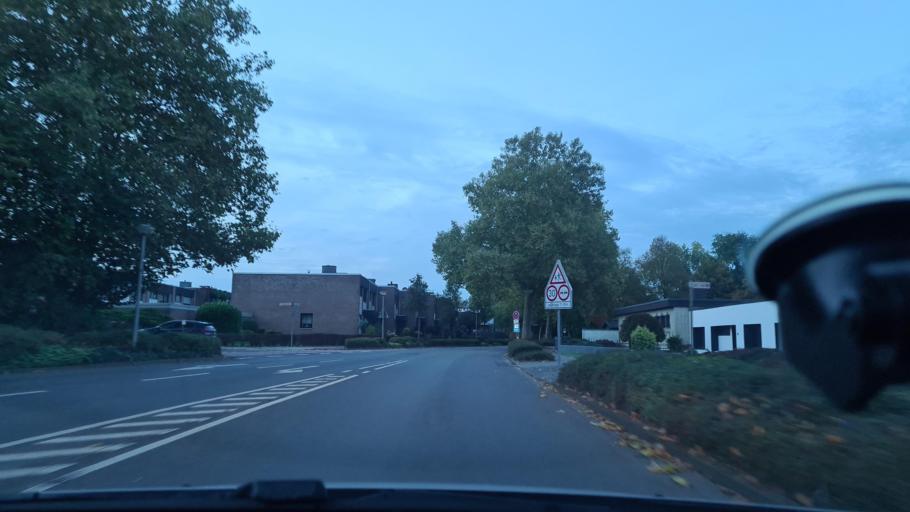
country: DE
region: North Rhine-Westphalia
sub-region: Regierungsbezirk Dusseldorf
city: Viersen
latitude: 51.2841
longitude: 6.3631
